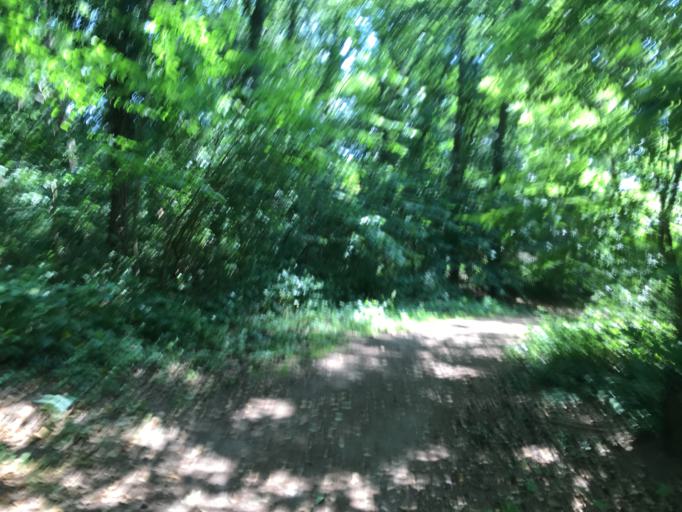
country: DE
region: Rheinland-Pfalz
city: Budenheim
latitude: 50.0056
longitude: 8.1897
